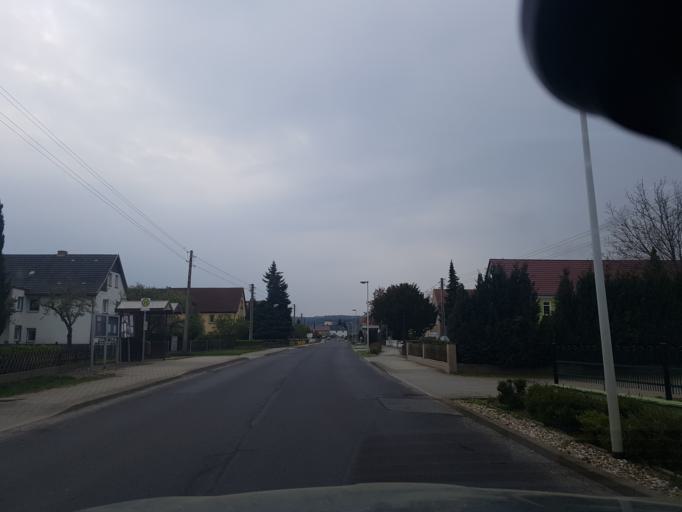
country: DE
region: Brandenburg
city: Grosskmehlen
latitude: 51.3868
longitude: 13.7113
